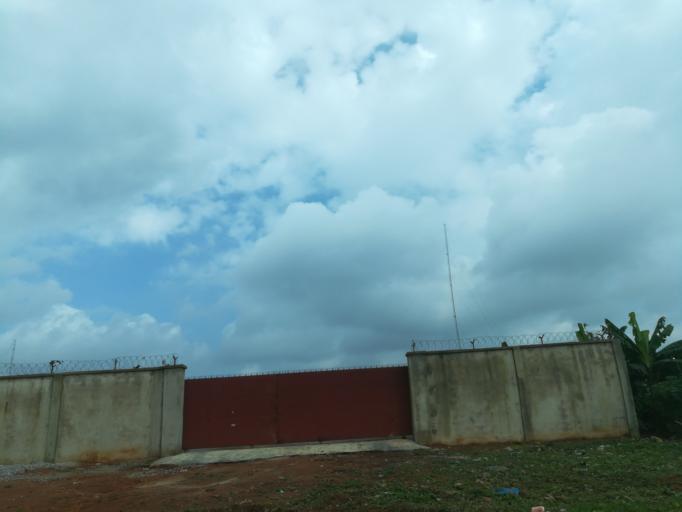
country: NG
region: Lagos
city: Ikorodu
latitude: 6.6561
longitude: 3.5822
